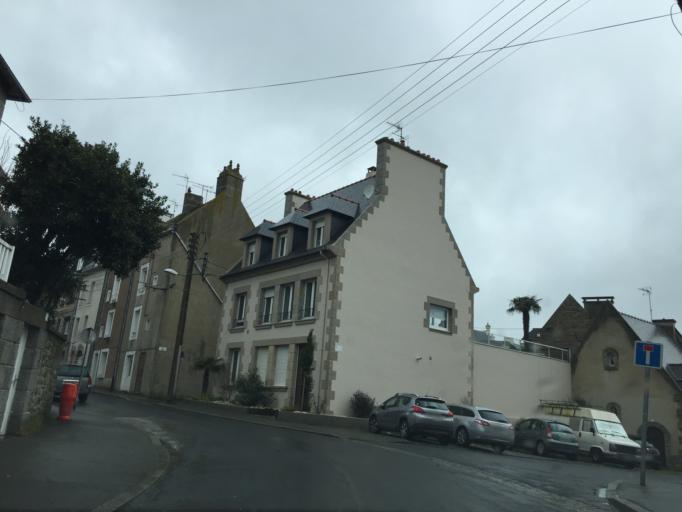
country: FR
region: Brittany
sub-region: Departement d'Ille-et-Vilaine
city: Saint-Malo
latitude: 48.6362
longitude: -2.0242
